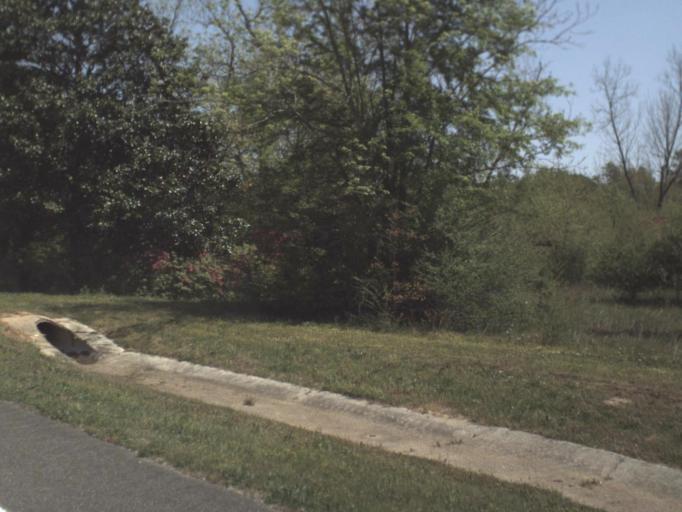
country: US
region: Alabama
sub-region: Escambia County
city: East Brewton
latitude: 30.8996
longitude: -87.0219
